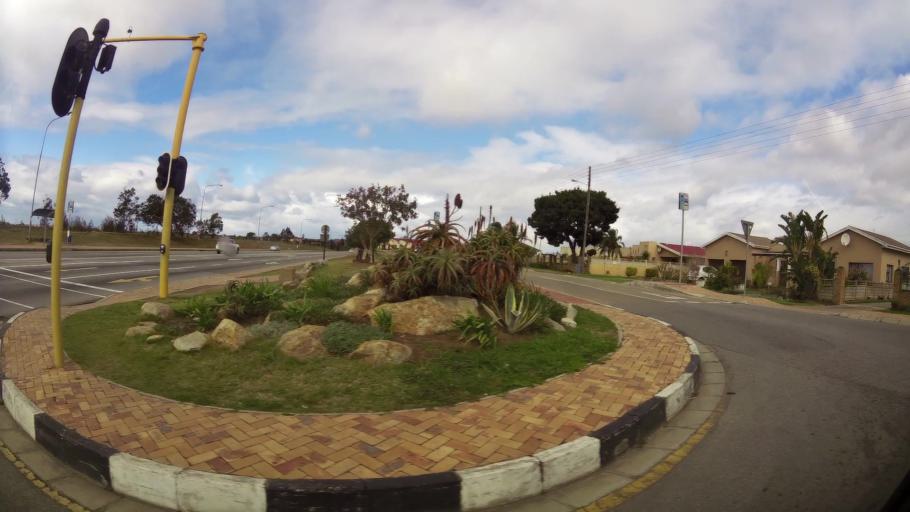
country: ZA
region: Western Cape
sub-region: Eden District Municipality
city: George
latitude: -34.0029
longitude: 22.4470
